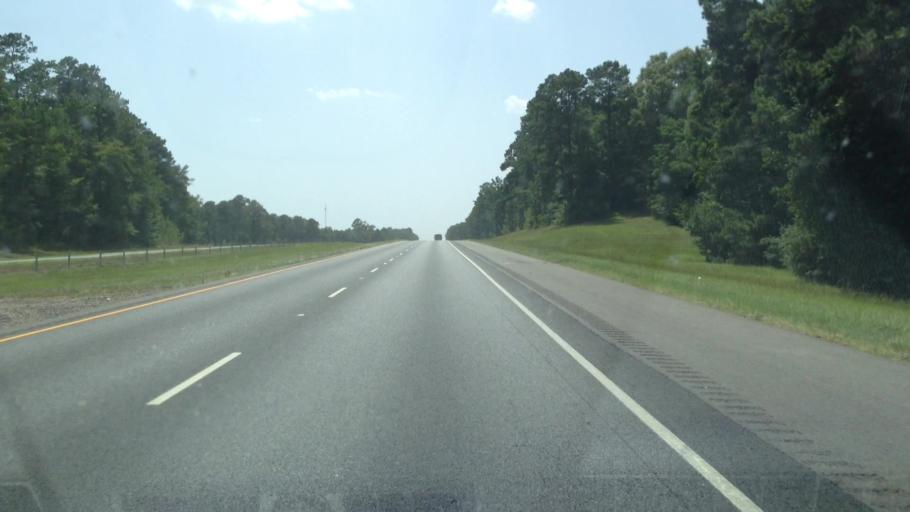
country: US
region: Louisiana
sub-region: Webster Parish
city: Minden
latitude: 32.5630
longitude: -93.1075
